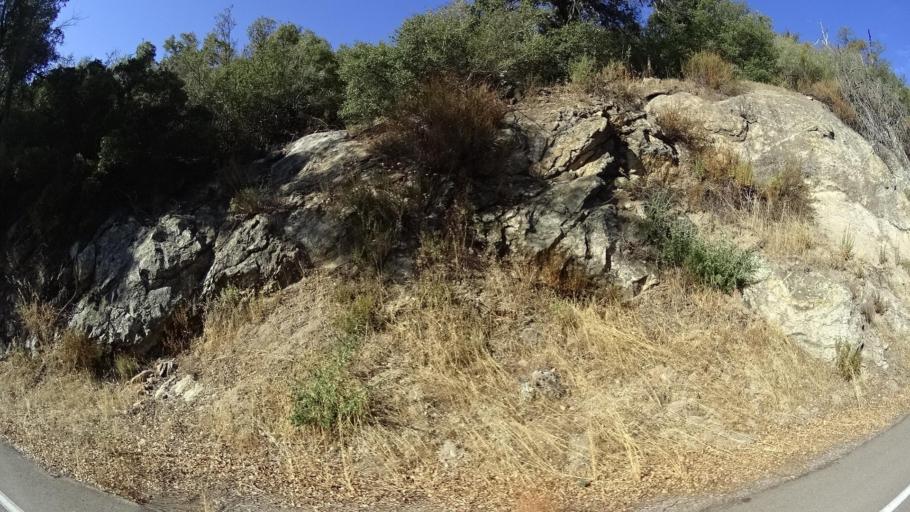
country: US
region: California
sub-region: Riverside County
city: Aguanga
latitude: 33.2613
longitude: -116.7650
